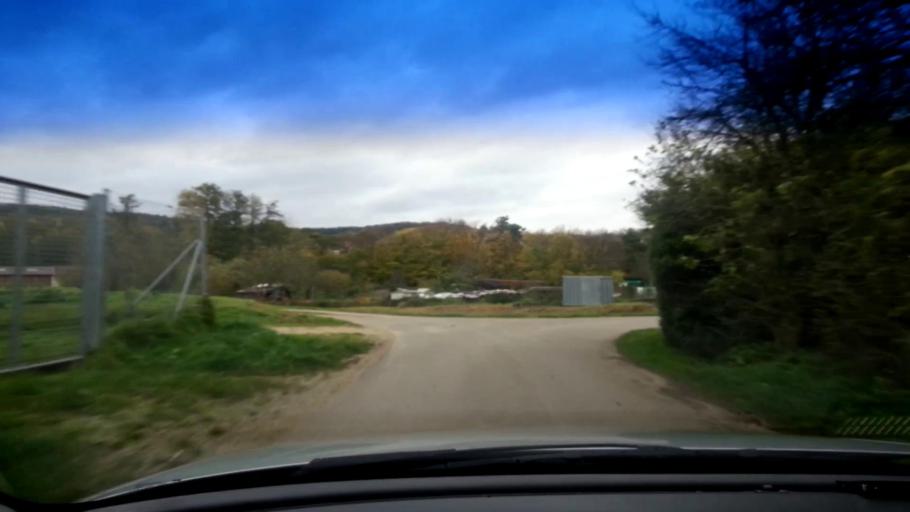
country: DE
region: Bavaria
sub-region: Upper Franconia
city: Hallstadt
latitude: 49.9292
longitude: 10.8532
